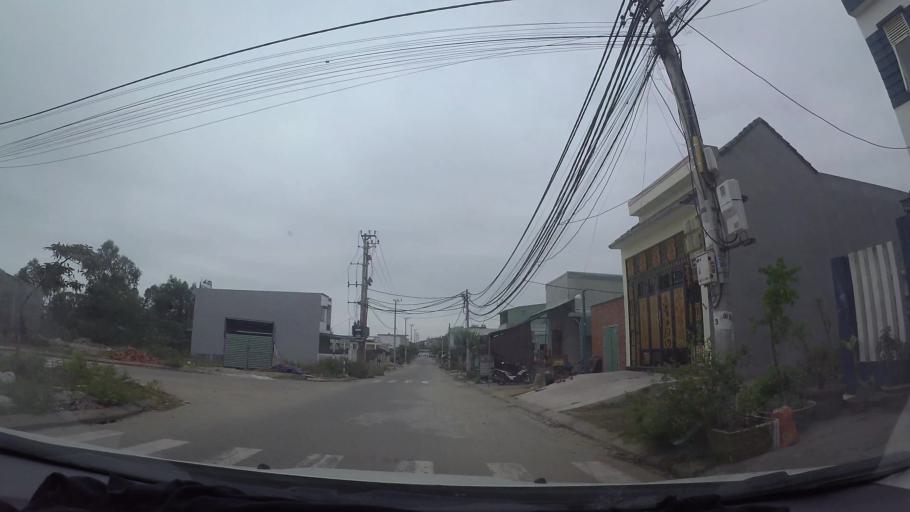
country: VN
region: Da Nang
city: Lien Chieu
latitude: 16.0704
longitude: 108.1398
